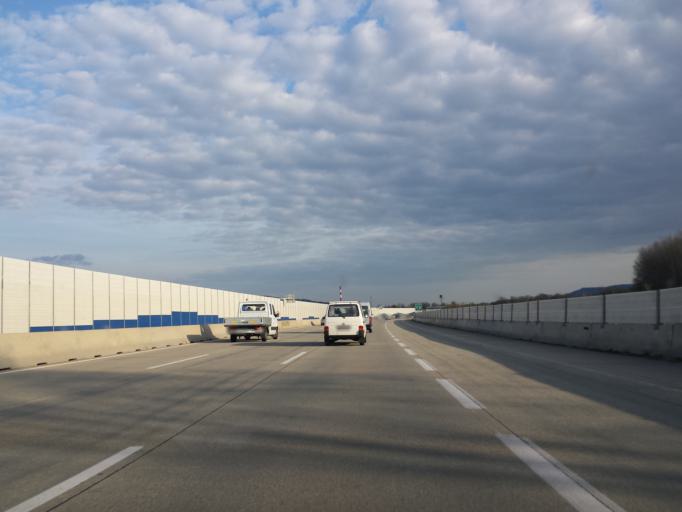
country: AT
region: Lower Austria
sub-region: Politischer Bezirk Korneuburg
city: Korneuburg
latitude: 48.3547
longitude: 16.3143
